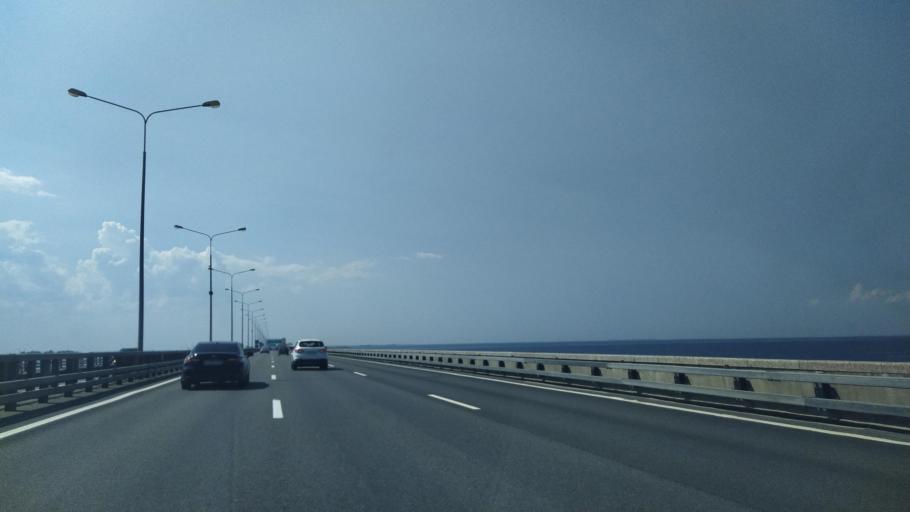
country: RU
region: Leningrad
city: Gorskaya
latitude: 60.0312
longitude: 29.8853
